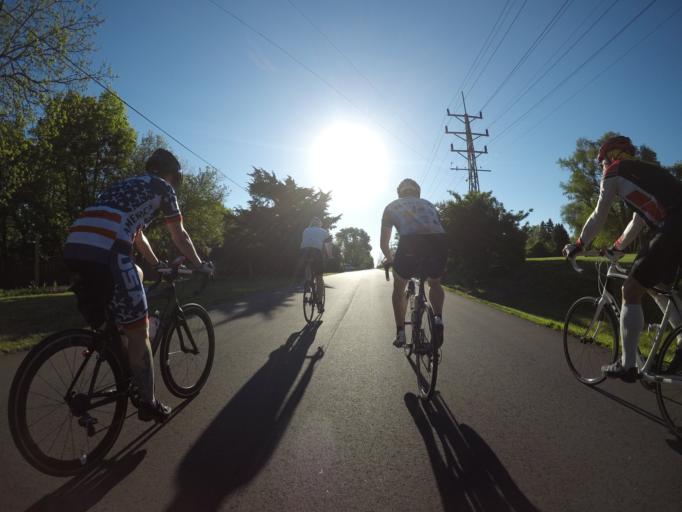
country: US
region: Kansas
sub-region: Shawnee County
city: Topeka
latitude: 39.0515
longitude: -95.6252
